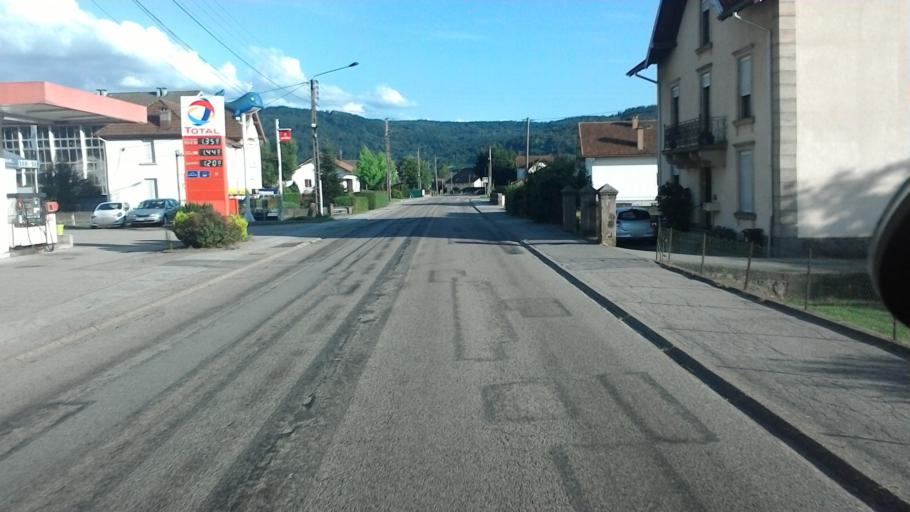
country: FR
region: Lorraine
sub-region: Departement des Vosges
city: Rupt-sur-Moselle
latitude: 47.9206
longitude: 6.6626
